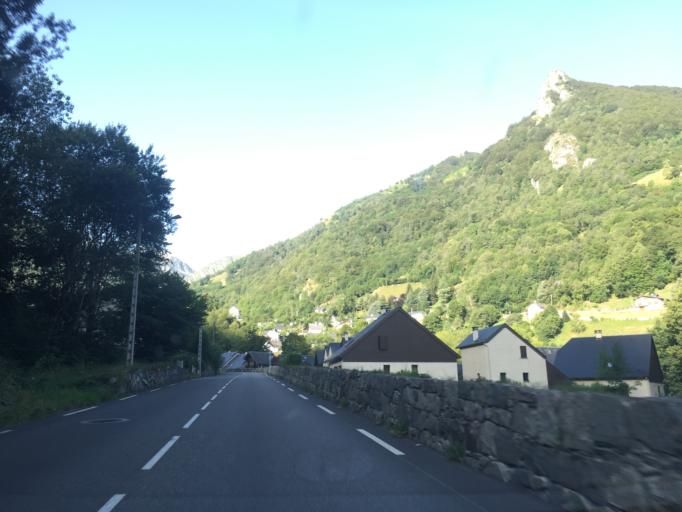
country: FR
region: Midi-Pyrenees
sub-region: Departement des Hautes-Pyrenees
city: Cauterets
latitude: 42.8994
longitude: -0.1093
